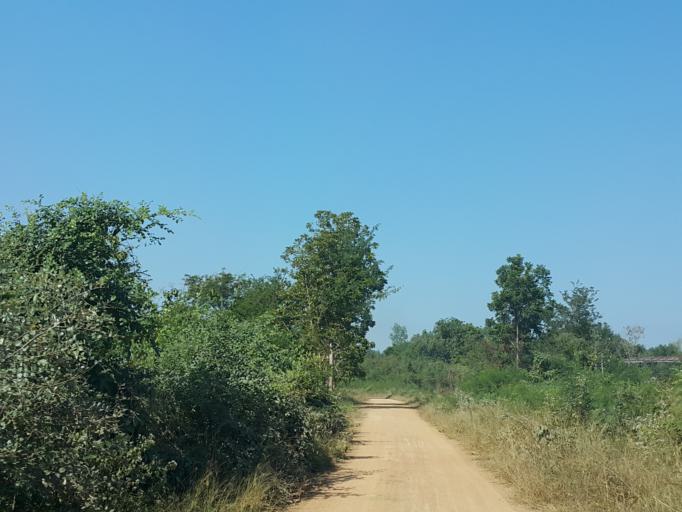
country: TH
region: Sukhothai
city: Thung Saliam
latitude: 17.3429
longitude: 99.4424
